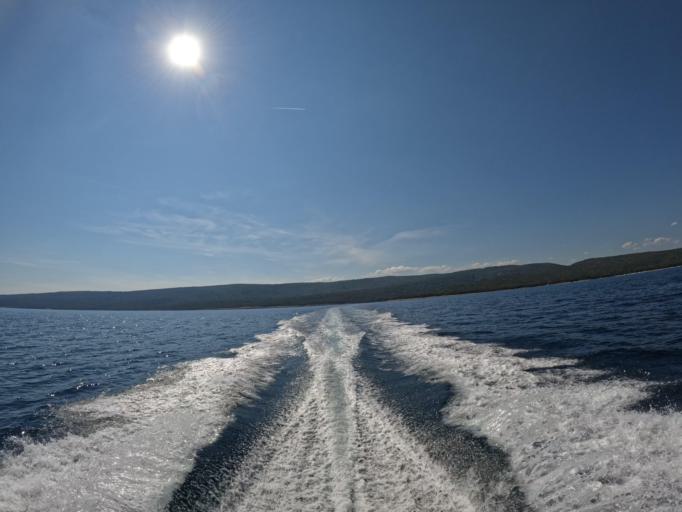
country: HR
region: Primorsko-Goranska
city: Cres
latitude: 44.9455
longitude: 14.4854
